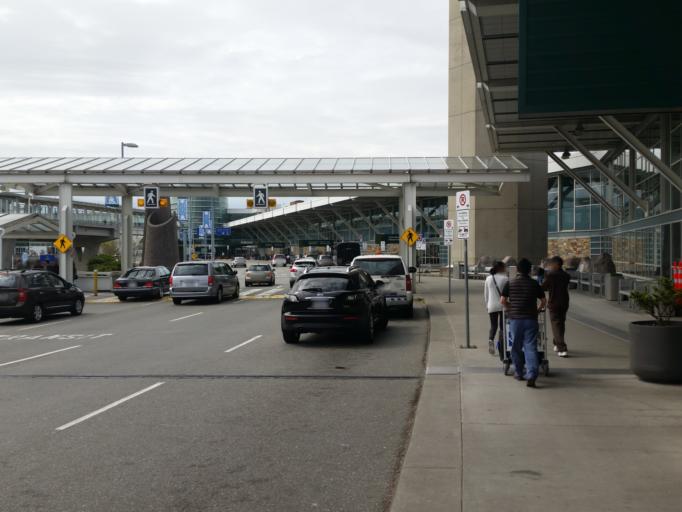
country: CA
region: British Columbia
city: Richmond
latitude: 49.1948
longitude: -123.1776
